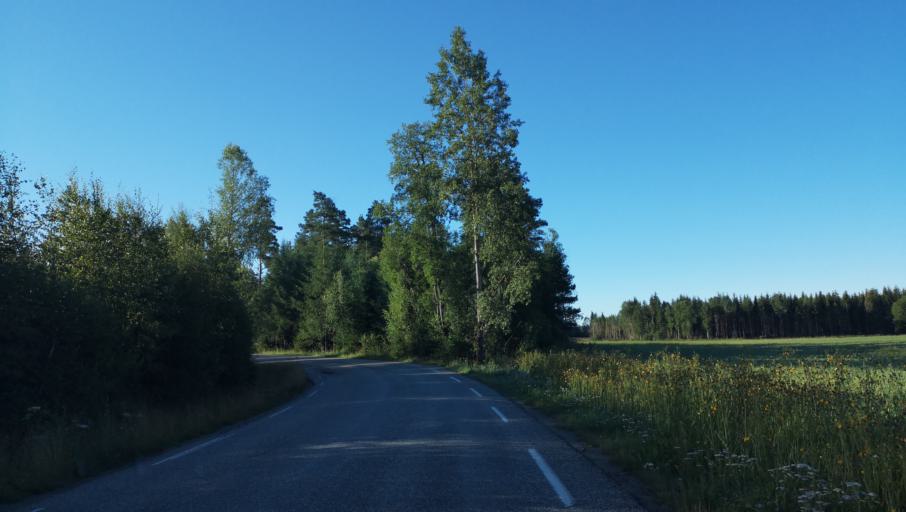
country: NO
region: Ostfold
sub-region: Hobol
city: Knappstad
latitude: 59.6394
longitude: 11.0167
